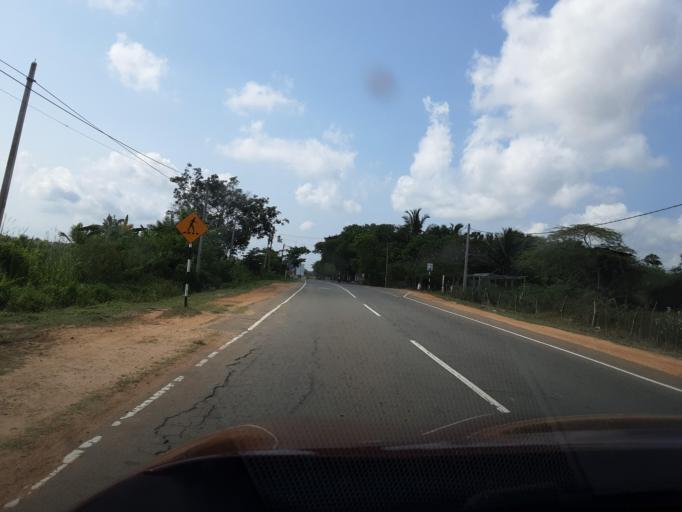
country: LK
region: Southern
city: Tangalla
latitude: 6.2370
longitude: 81.2274
